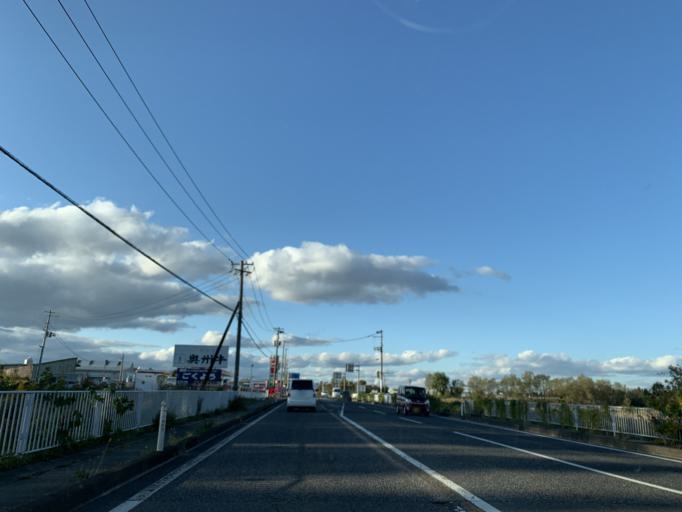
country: JP
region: Iwate
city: Kitakami
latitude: 39.2157
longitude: 141.1022
